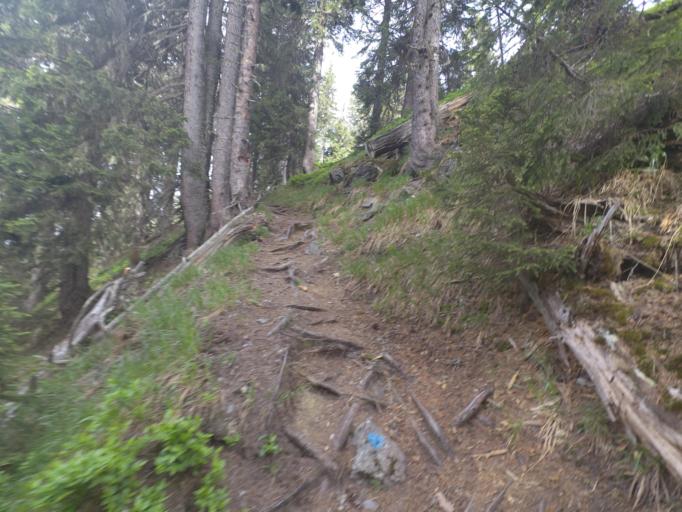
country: AT
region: Salzburg
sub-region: Politischer Bezirk Sankt Johann im Pongau
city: Muhlbach am Hochkonig
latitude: 47.3686
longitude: 13.0843
